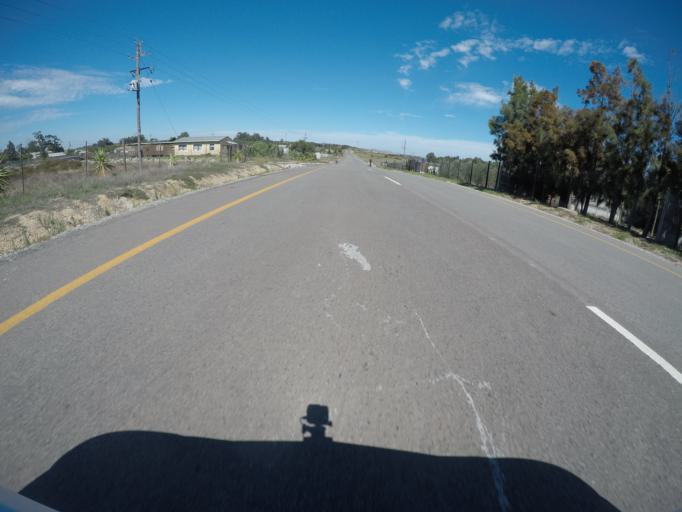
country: ZA
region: Western Cape
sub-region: West Coast District Municipality
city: Malmesbury
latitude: -33.5797
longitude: 18.6469
